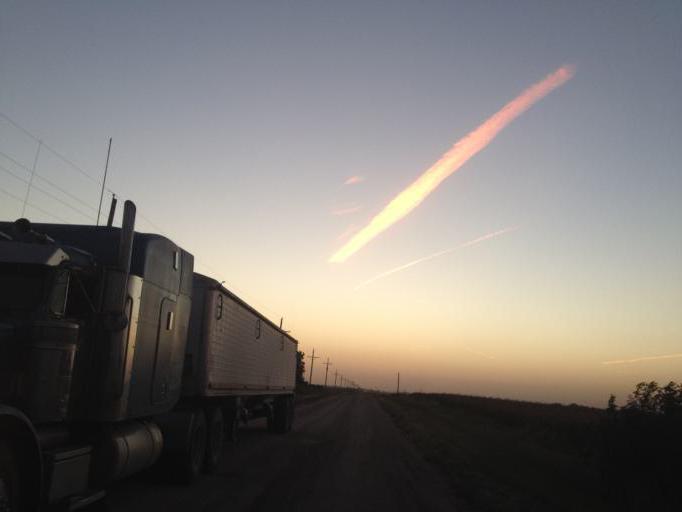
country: US
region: Kansas
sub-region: Rice County
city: Lyons
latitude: 38.3913
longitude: -98.3568
